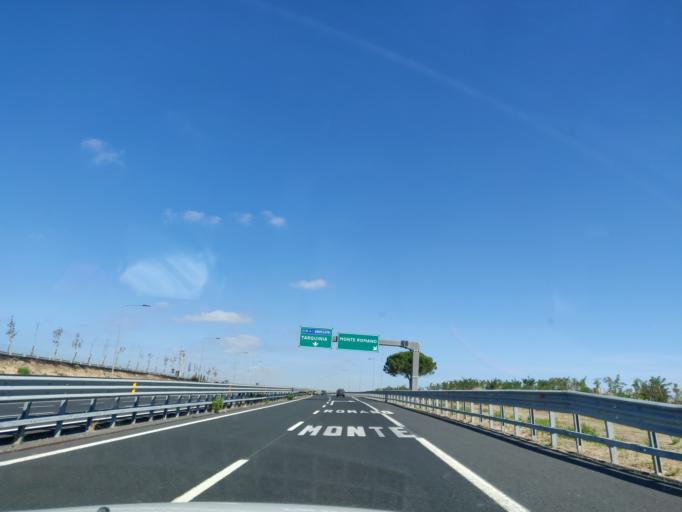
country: IT
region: Latium
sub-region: Provincia di Viterbo
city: Tarquinia
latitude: 42.2078
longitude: 11.7835
